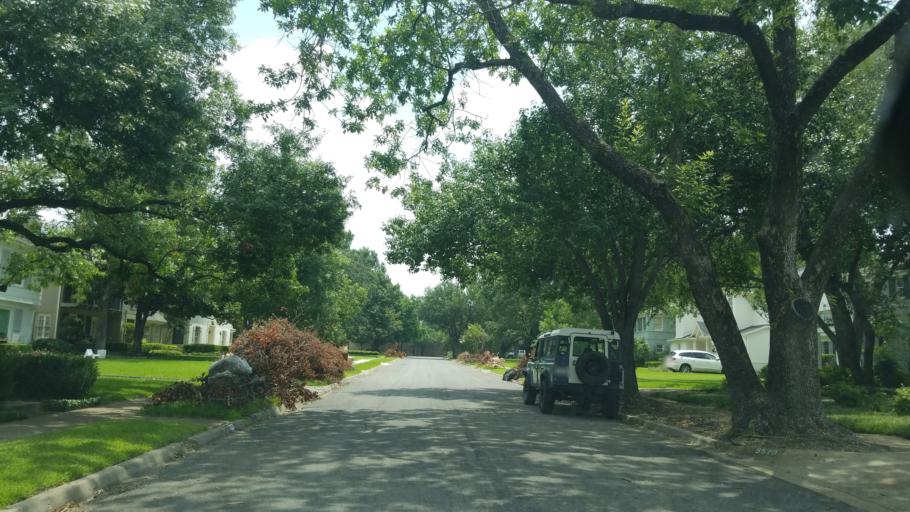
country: US
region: Texas
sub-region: Dallas County
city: University Park
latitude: 32.8465
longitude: -96.8159
